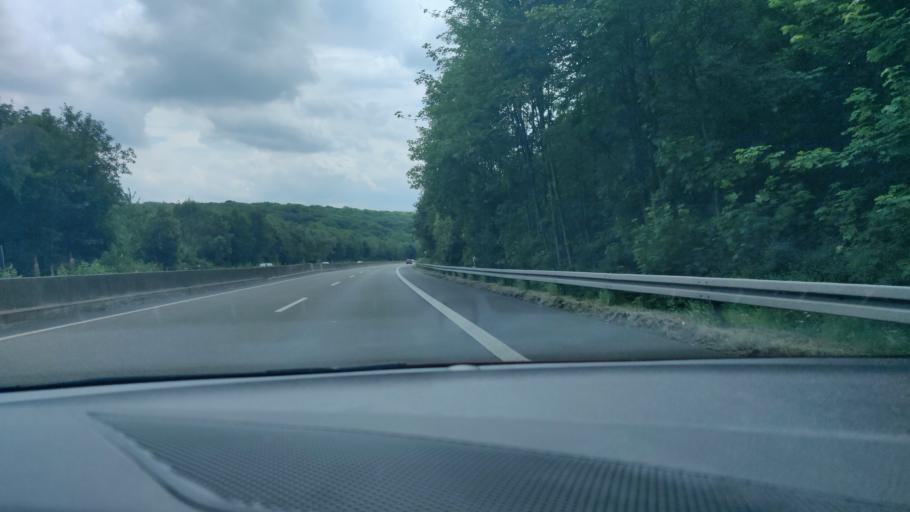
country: DE
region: North Rhine-Westphalia
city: Wulfrath
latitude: 51.2937
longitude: 7.0691
